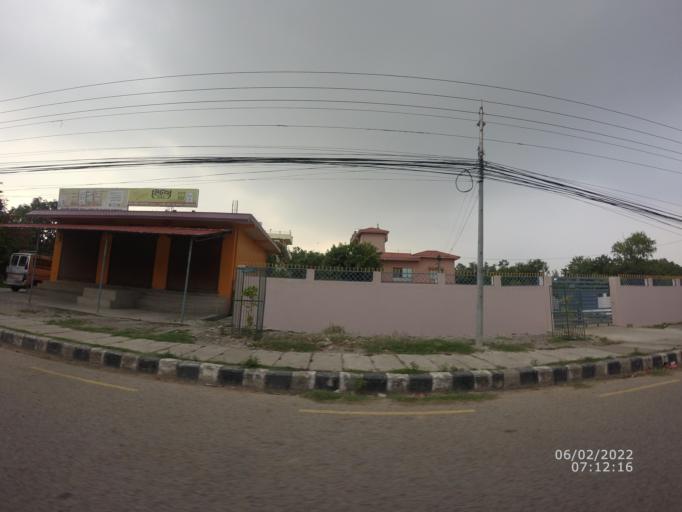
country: NP
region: Western Region
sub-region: Lumbini Zone
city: Bhairahawa
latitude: 27.4853
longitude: 83.4417
